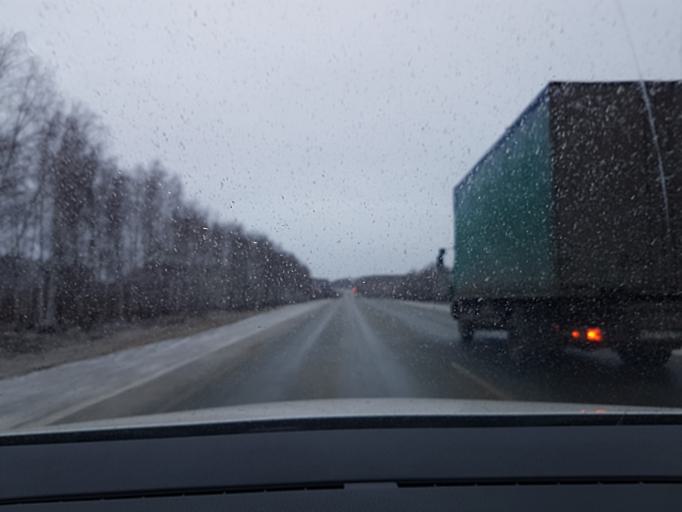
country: RU
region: Tambov
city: Michurinsk
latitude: 53.0181
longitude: 40.5247
